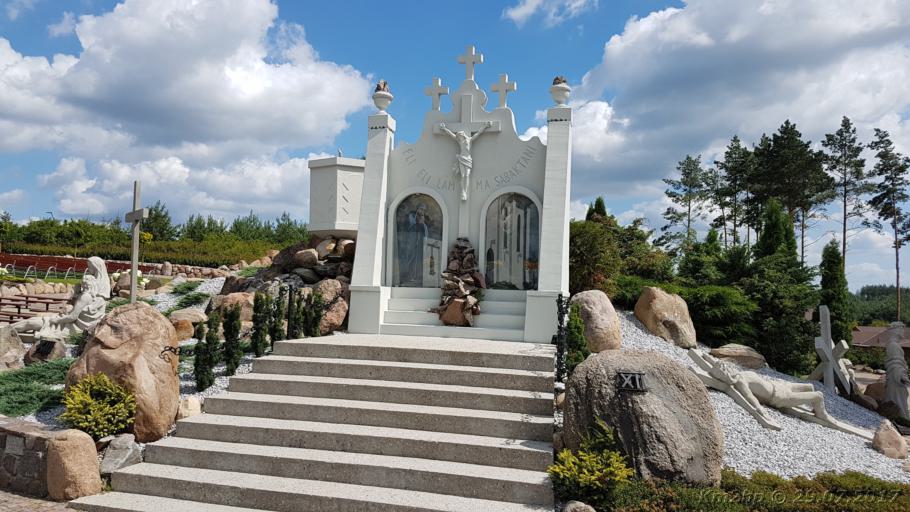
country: PL
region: Podlasie
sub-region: Powiat bialostocki
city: Wasilkow
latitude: 53.2208
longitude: 23.2228
